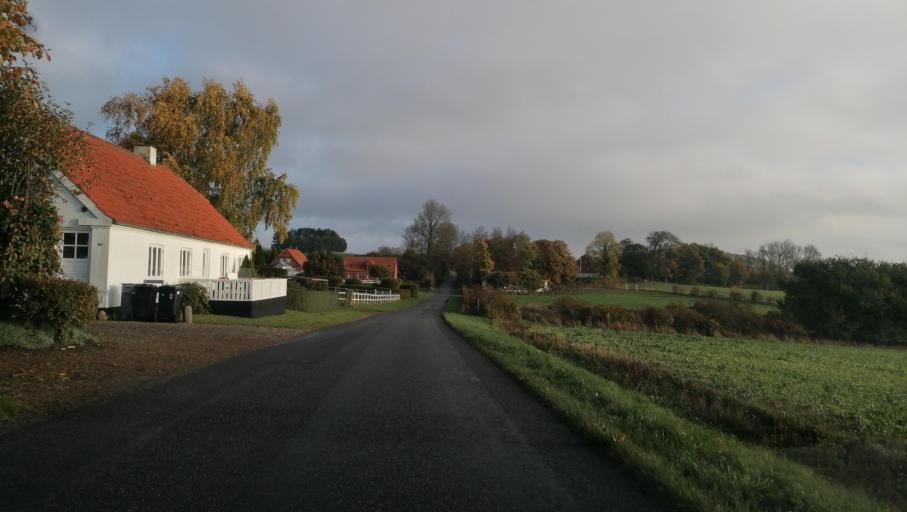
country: DK
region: Zealand
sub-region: Odsherred Kommune
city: Horve
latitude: 55.7338
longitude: 11.3975
